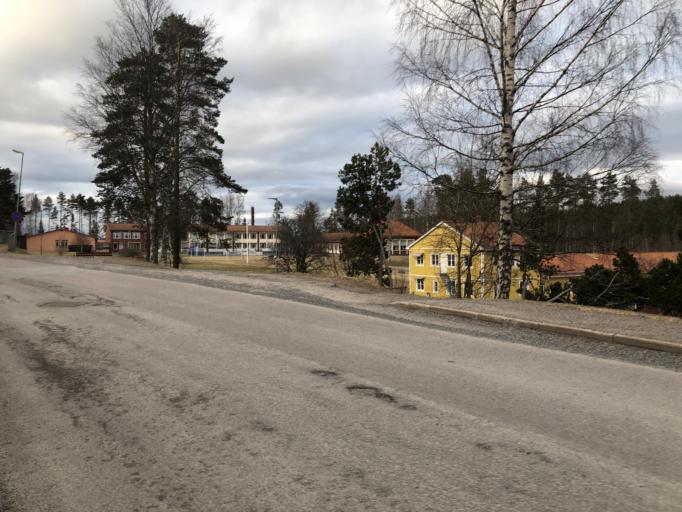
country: SE
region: Vaermland
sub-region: Filipstads Kommun
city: Lesjofors
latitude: 59.9836
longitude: 14.1742
